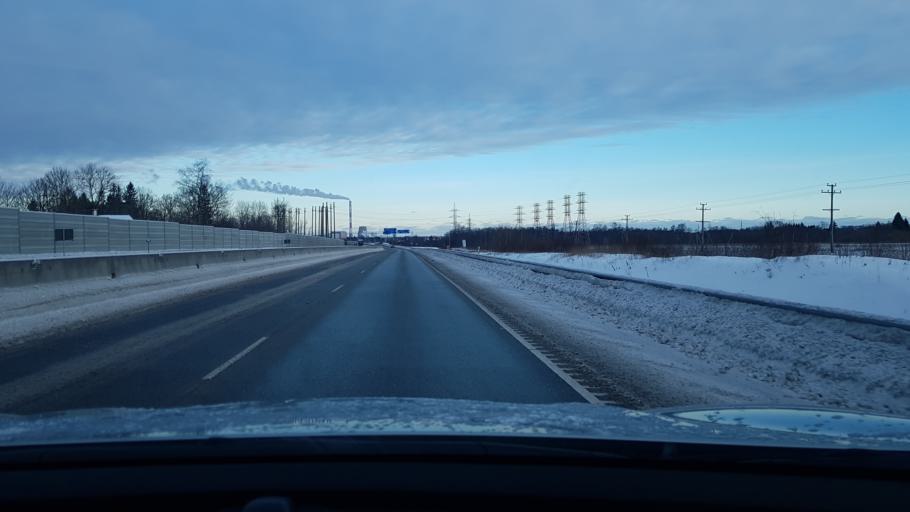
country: EE
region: Harju
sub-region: Joelaehtme vald
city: Loo
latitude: 59.4188
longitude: 24.9204
